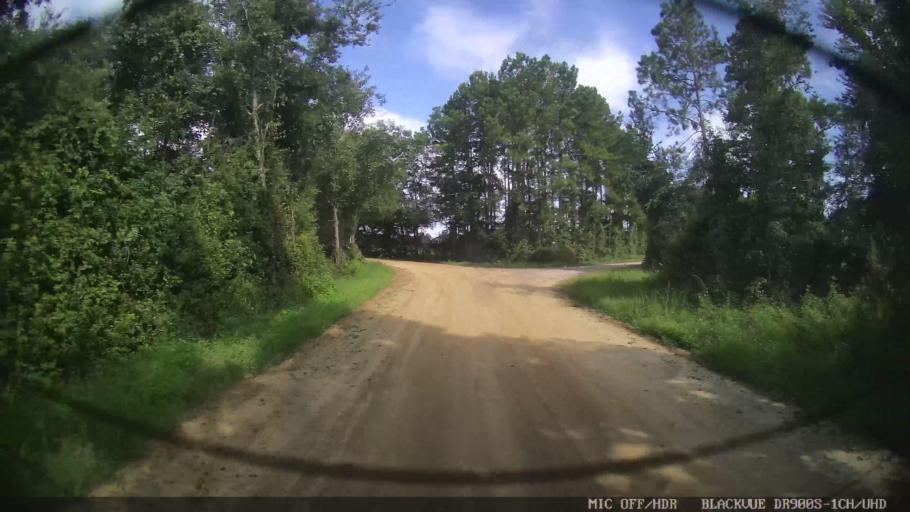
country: US
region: Georgia
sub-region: Echols County
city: Statenville
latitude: 30.6276
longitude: -83.1877
